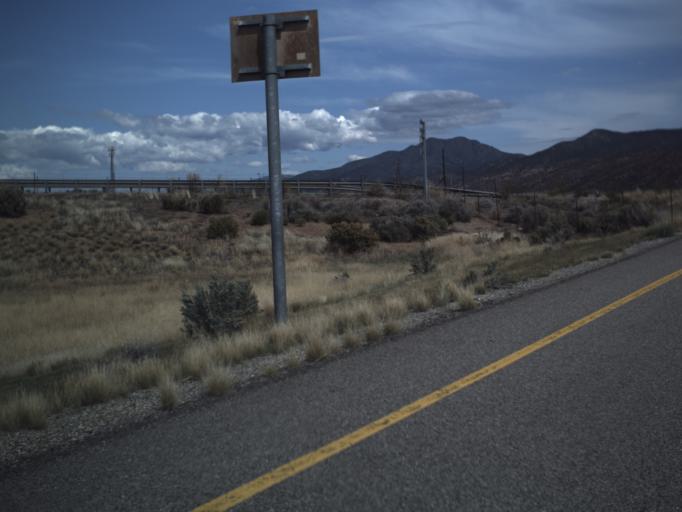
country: US
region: Utah
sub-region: Iron County
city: Parowan
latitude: 37.9075
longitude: -112.7768
